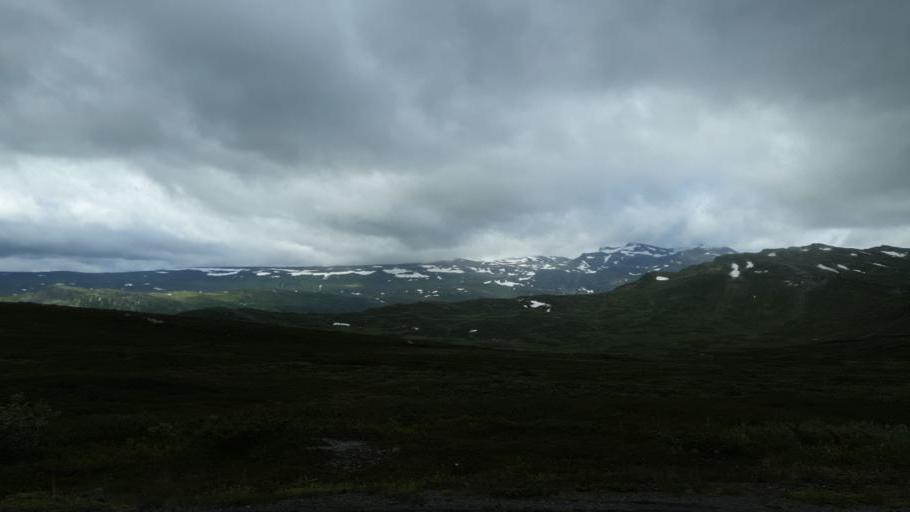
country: NO
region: Oppland
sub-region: Vestre Slidre
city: Slidre
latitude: 61.2849
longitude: 8.8280
